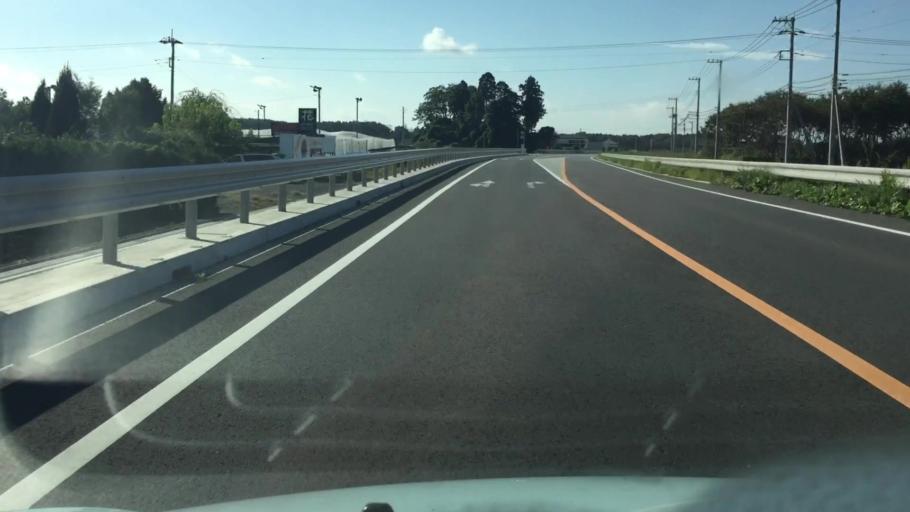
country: JP
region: Tochigi
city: Ujiie
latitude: 36.5944
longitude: 139.9852
